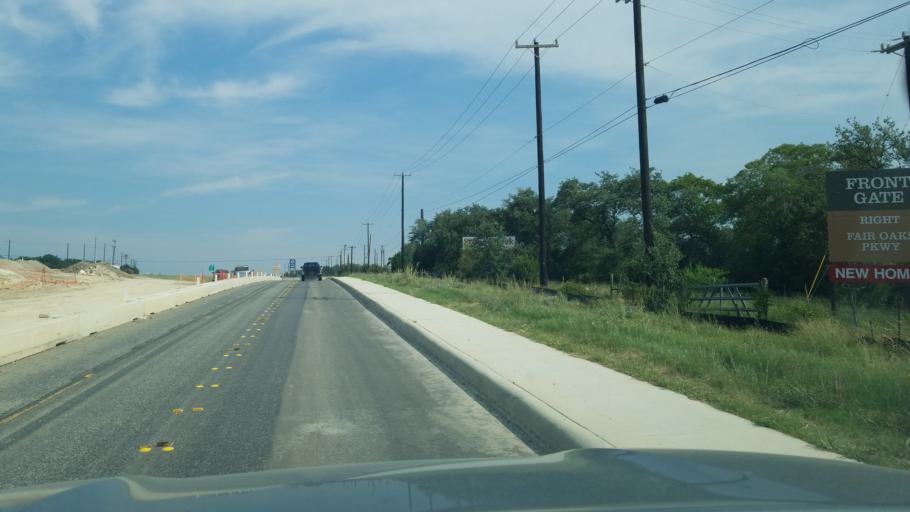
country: US
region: Texas
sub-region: Bexar County
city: Scenic Oaks
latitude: 29.7145
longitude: -98.6614
